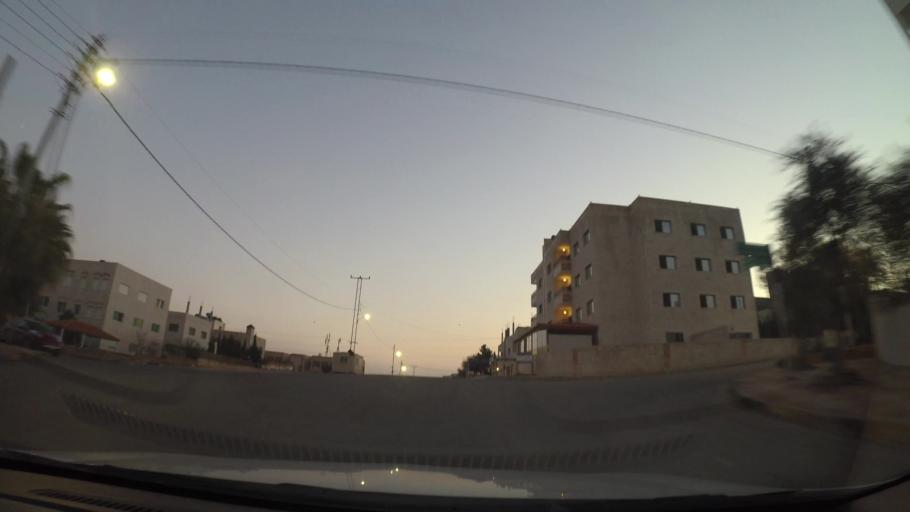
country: JO
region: Amman
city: Al Bunayyat ash Shamaliyah
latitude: 31.8872
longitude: 35.9235
